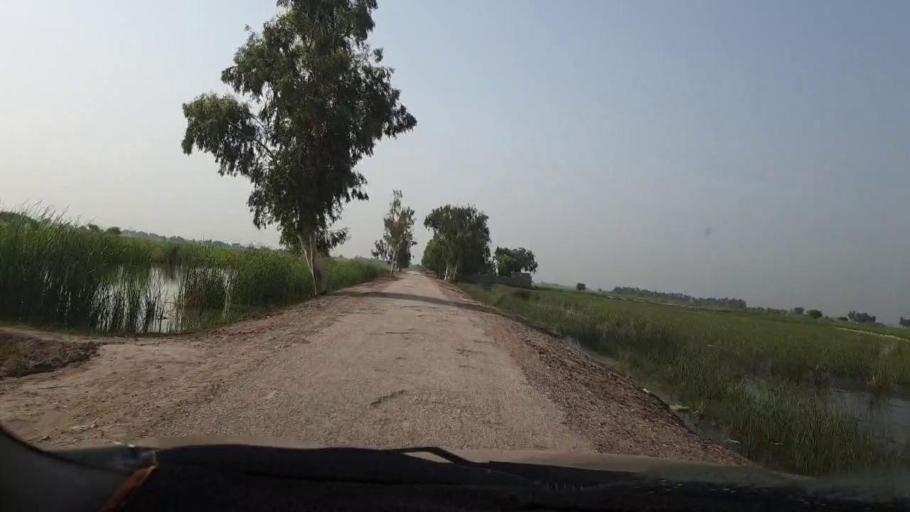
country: PK
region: Sindh
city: Goth Garelo
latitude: 27.4751
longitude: 68.0869
